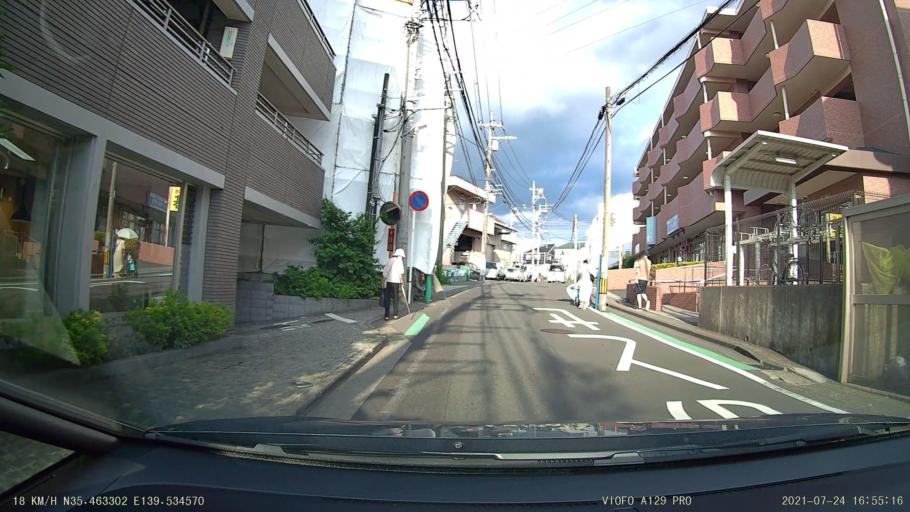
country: JP
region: Kanagawa
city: Minami-rinkan
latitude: 35.4633
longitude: 139.5346
